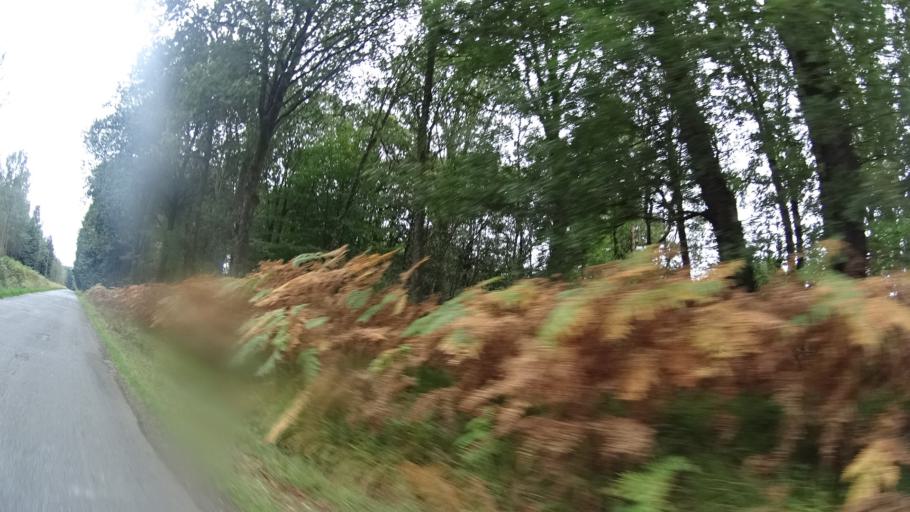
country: FR
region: Brittany
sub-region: Departement d'Ille-et-Vilaine
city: Paimpont
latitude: 48.0285
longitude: -2.1786
